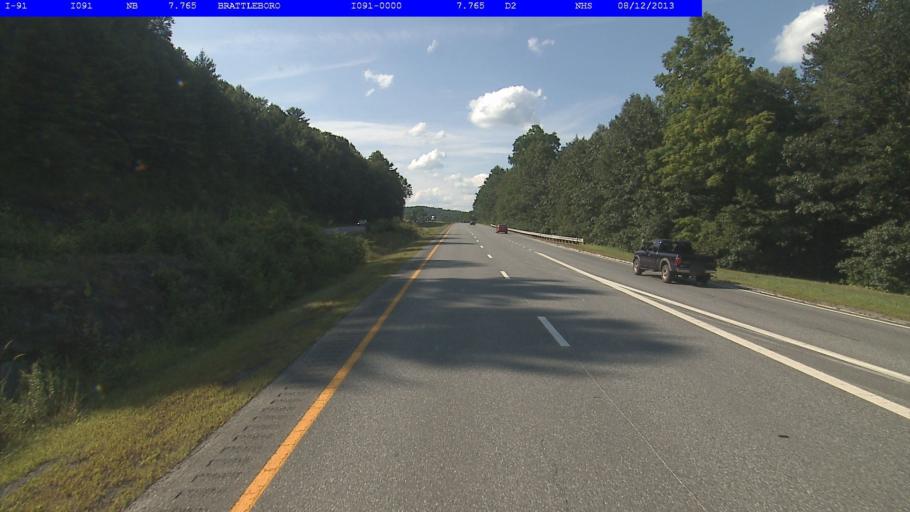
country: US
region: Vermont
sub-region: Windham County
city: Brattleboro
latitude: 42.8392
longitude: -72.5692
